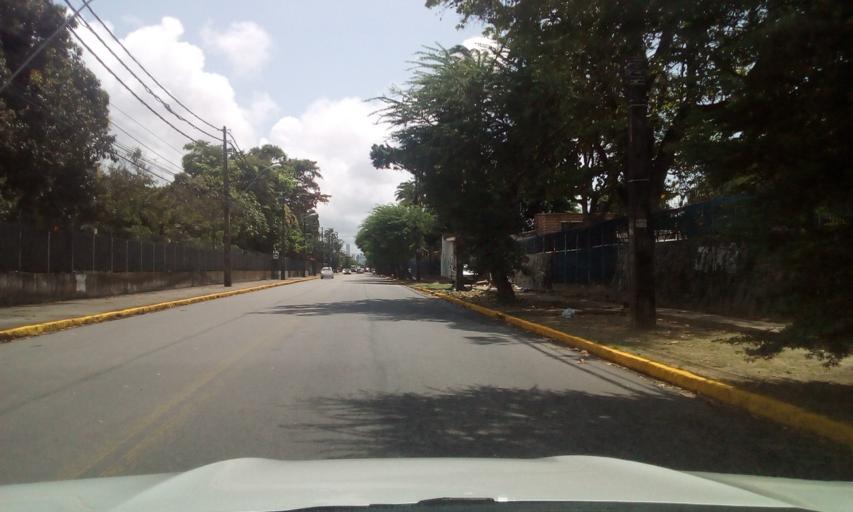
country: BR
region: Pernambuco
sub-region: Recife
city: Recife
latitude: -8.0628
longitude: -34.9265
